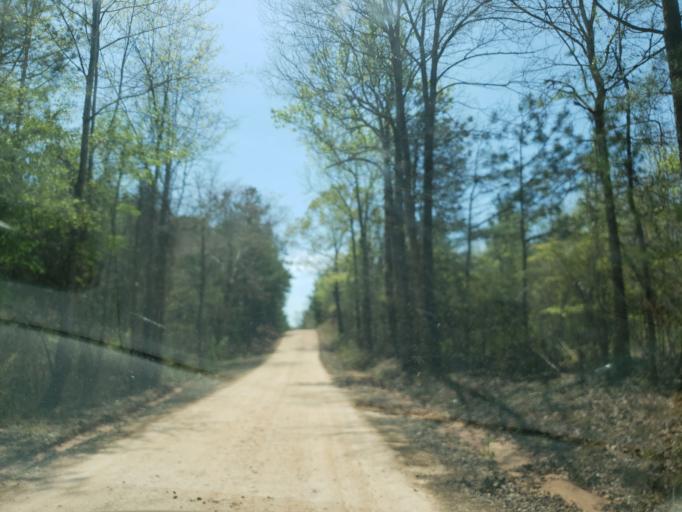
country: US
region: Alabama
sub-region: Tallapoosa County
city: Camp Hill
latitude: 32.6613
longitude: -85.6622
